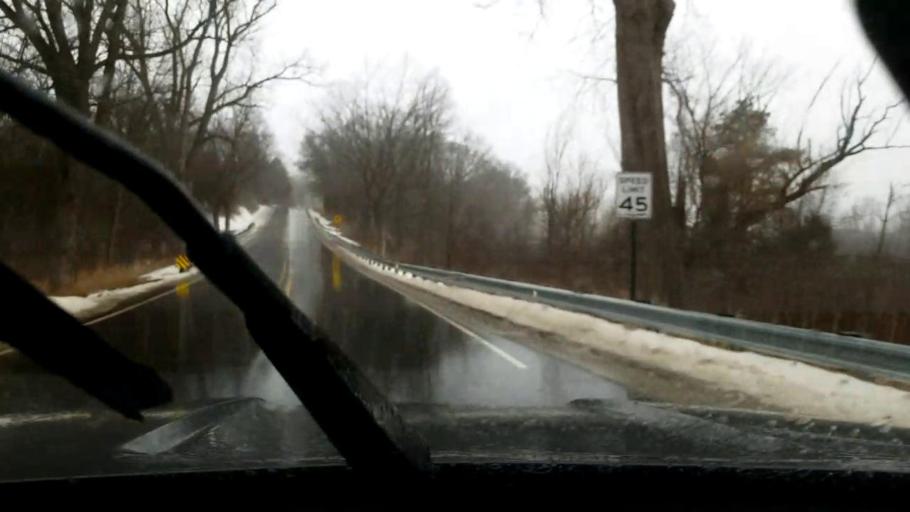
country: US
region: Michigan
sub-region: Jackson County
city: Grass Lake
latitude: 42.3355
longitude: -84.1796
